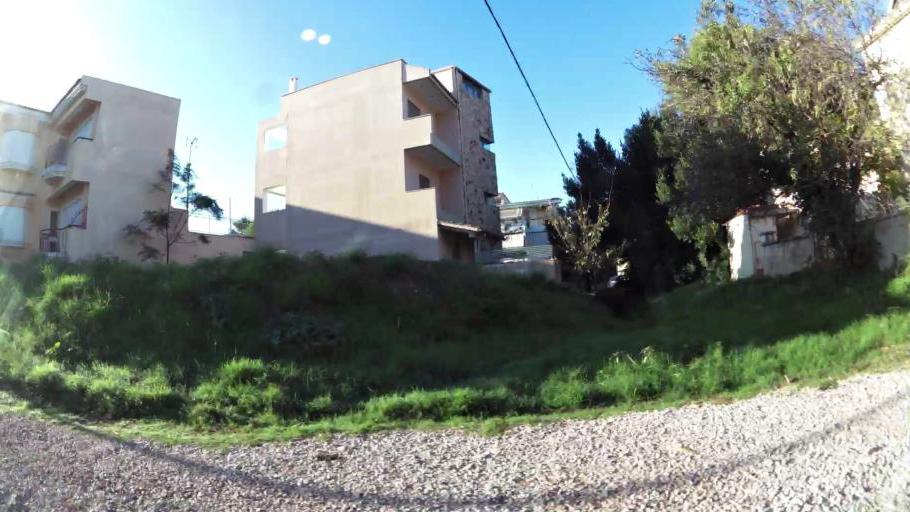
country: GR
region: Attica
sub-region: Nomarchia Athinas
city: Vrilissia
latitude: 38.0324
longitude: 23.8402
